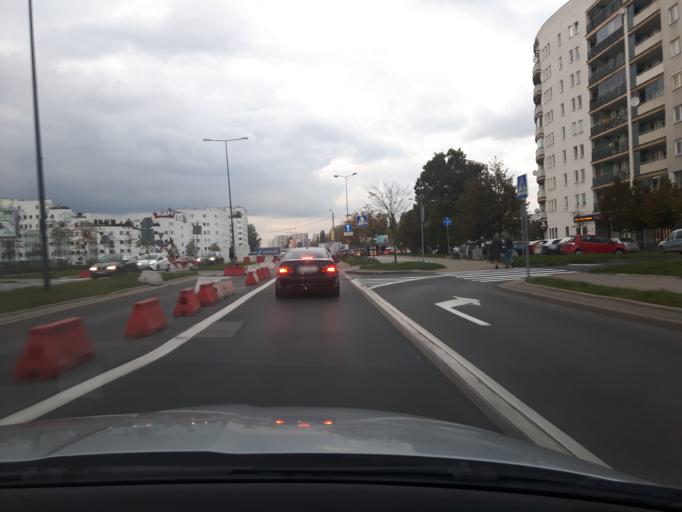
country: PL
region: Masovian Voivodeship
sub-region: Warszawa
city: Ursynow
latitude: 52.1441
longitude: 21.0534
